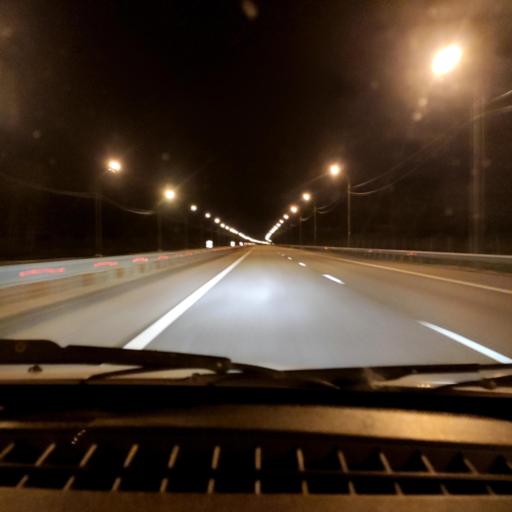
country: RU
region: Lipetsk
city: Zadonsk
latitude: 52.3362
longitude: 38.9817
